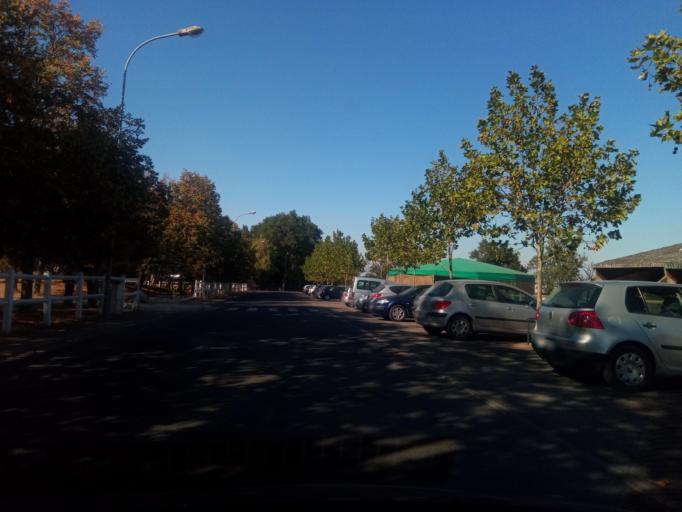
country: FR
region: Poitou-Charentes
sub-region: Departement de la Vienne
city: Montmorillon
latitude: 46.4160
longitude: 0.8442
